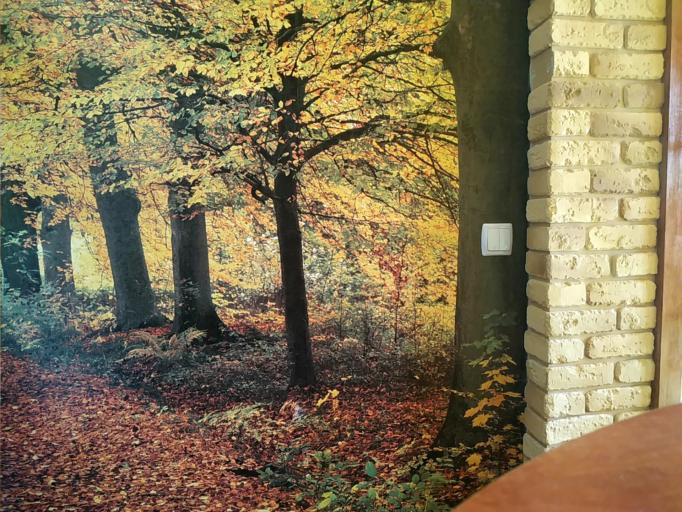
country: RU
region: Jaroslavl
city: Kukoboy
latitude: 58.9001
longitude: 39.6940
